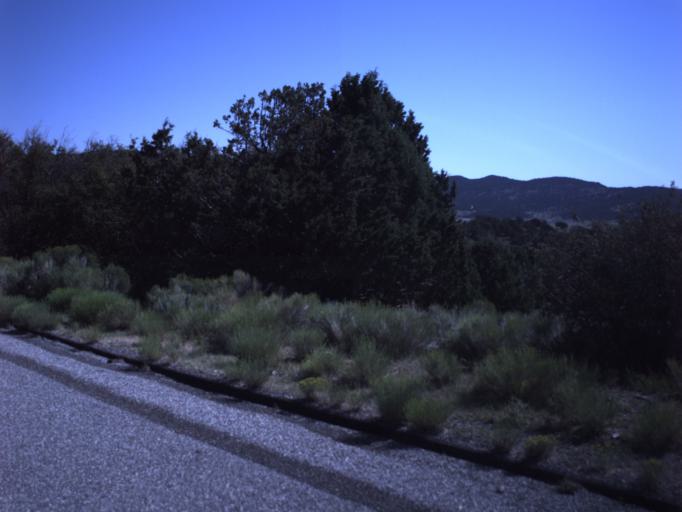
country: US
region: Utah
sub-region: Wayne County
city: Loa
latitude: 38.6214
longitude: -111.4548
